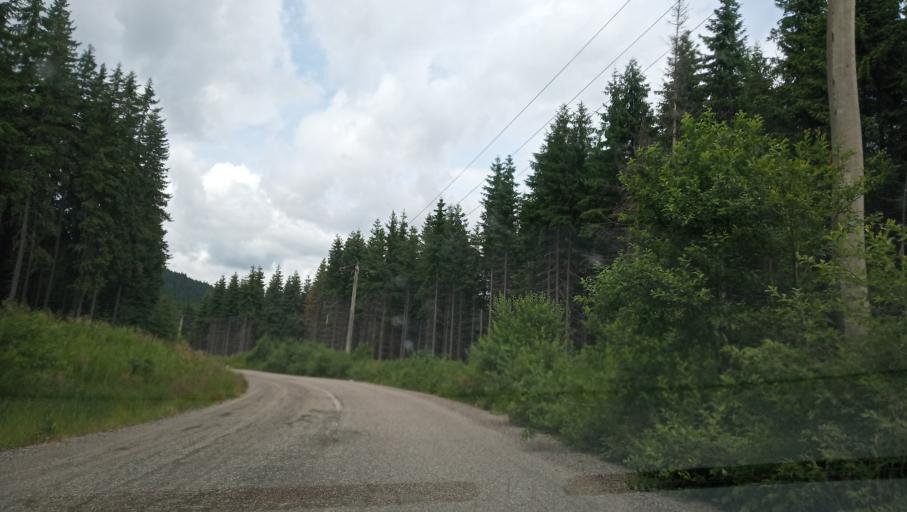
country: RO
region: Gorj
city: Novaci-Straini
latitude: 45.4197
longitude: 23.7052
